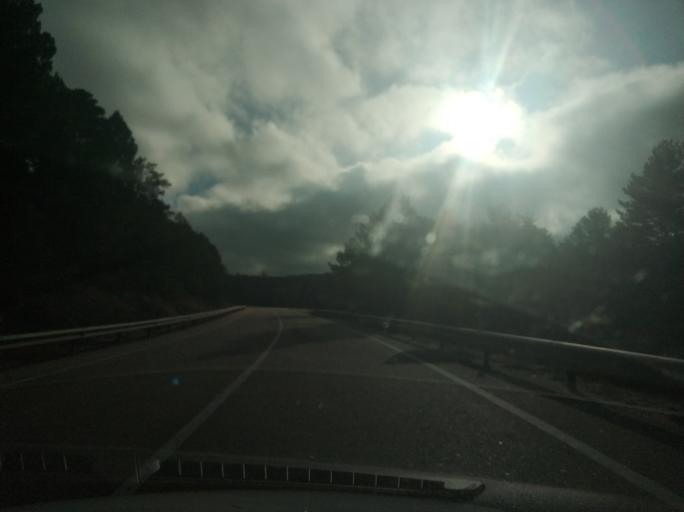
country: ES
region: Castille and Leon
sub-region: Provincia de Soria
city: Navaleno
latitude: 41.8345
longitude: -2.9992
